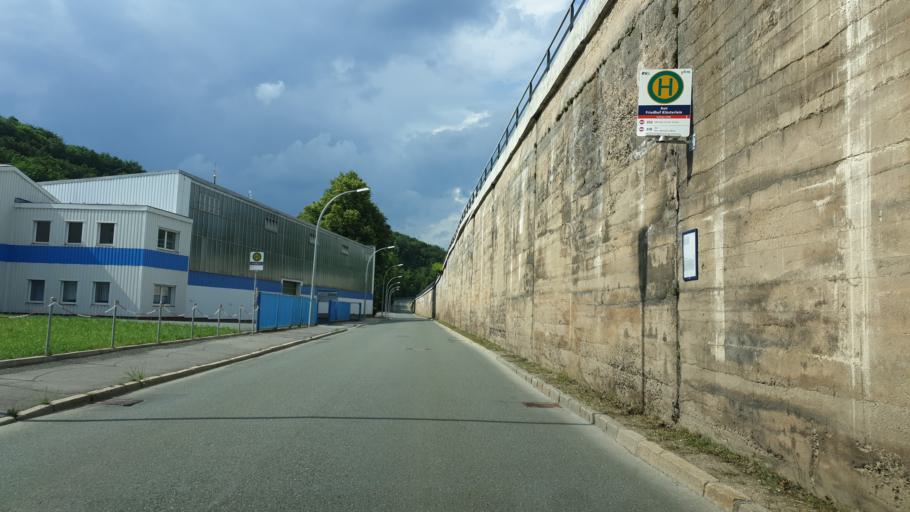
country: DE
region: Saxony
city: Aue
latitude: 50.5969
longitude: 12.6941
